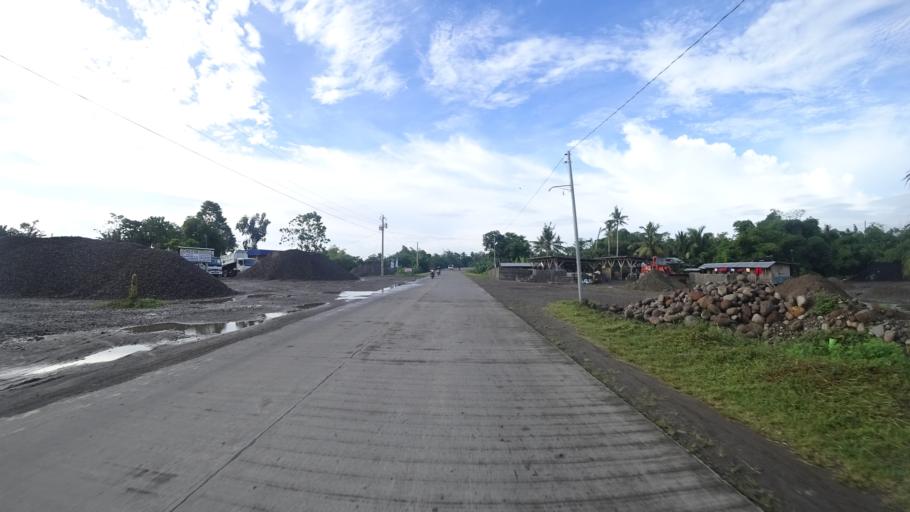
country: PH
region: Eastern Visayas
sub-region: Province of Leyte
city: Palo
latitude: 11.1622
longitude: 125.0027
